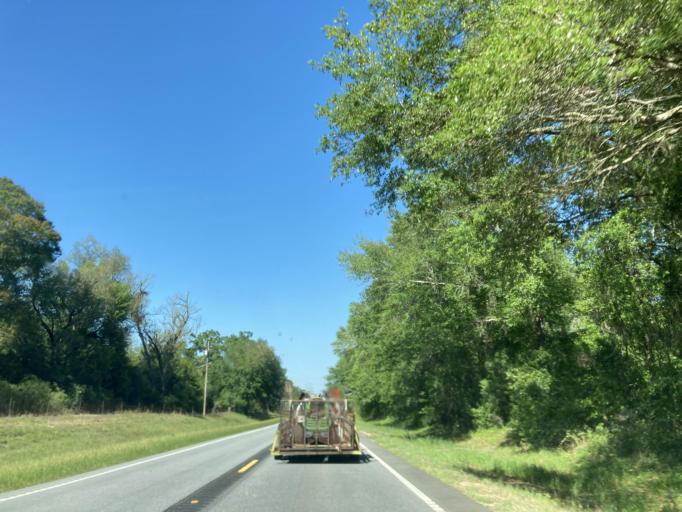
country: US
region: Georgia
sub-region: Baker County
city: Newton
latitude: 31.4385
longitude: -84.2727
